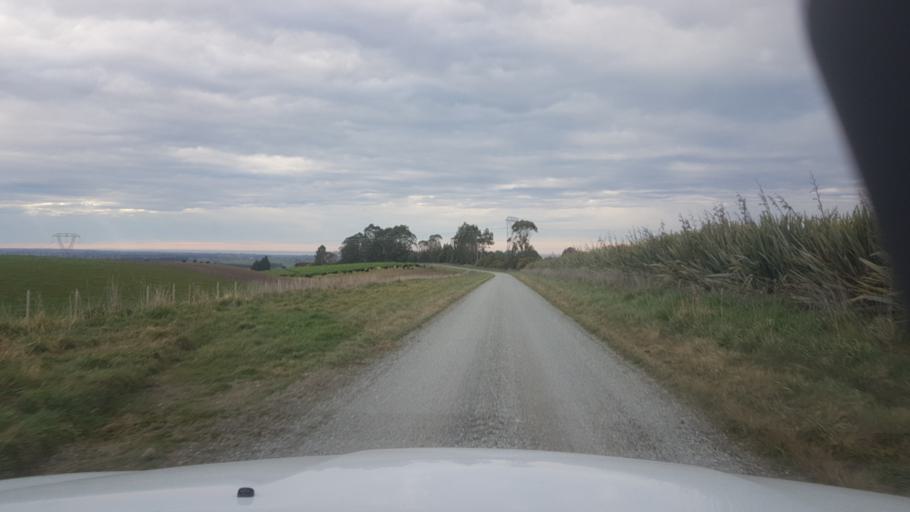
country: NZ
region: Canterbury
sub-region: Timaru District
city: Pleasant Point
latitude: -44.3457
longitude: 171.1299
